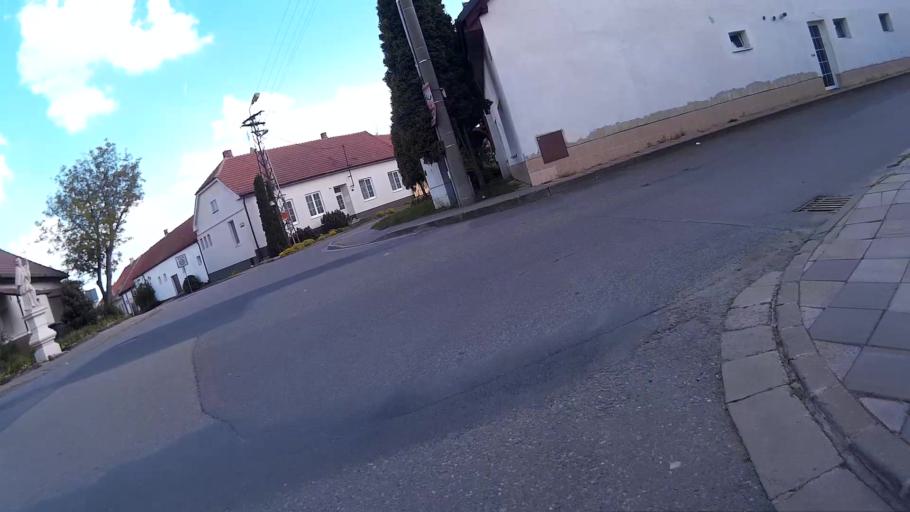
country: CZ
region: South Moravian
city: Modrice
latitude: 49.1266
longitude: 16.6133
